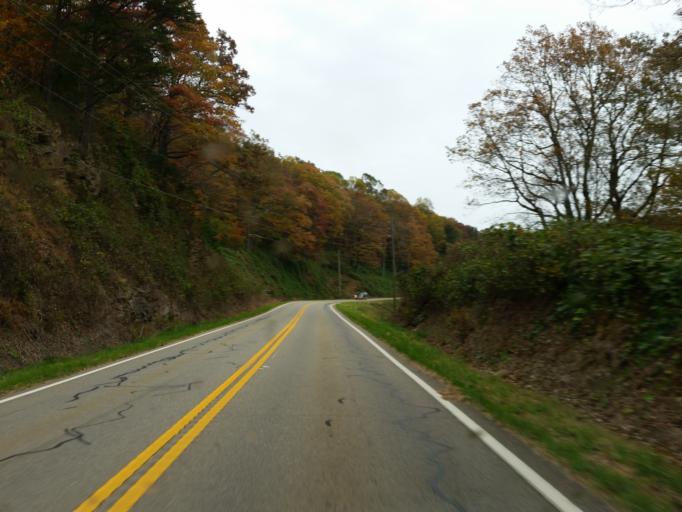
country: US
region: Georgia
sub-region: Pickens County
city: Jasper
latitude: 34.5336
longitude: -84.3806
